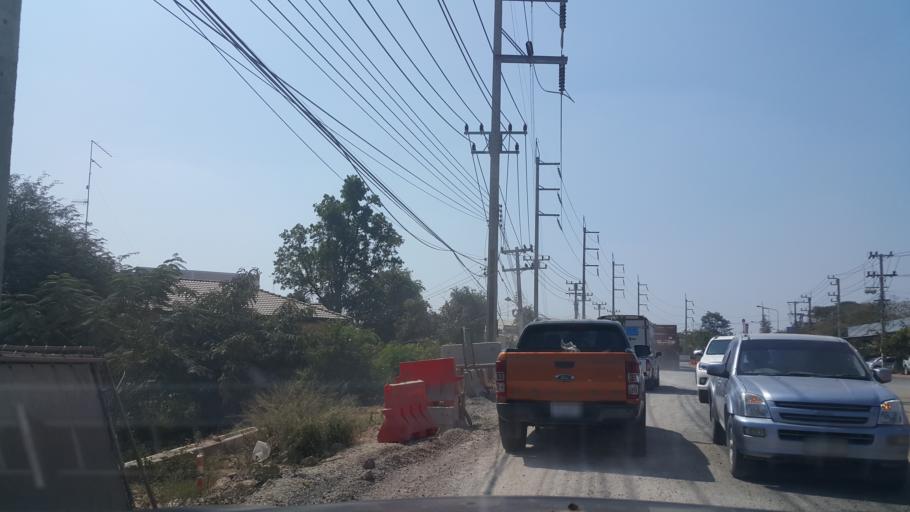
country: TH
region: Nakhon Ratchasima
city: Bua Yai
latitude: 15.5923
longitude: 102.4276
